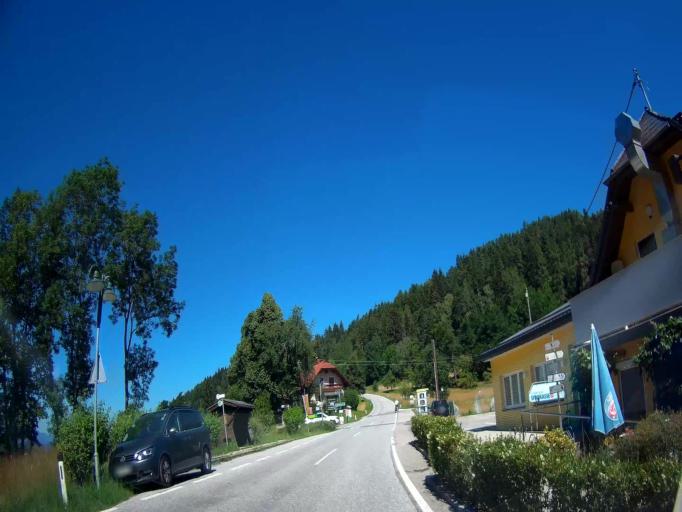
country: AT
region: Carinthia
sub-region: Politischer Bezirk Klagenfurt Land
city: Maria Worth
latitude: 46.6021
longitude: 14.1446
